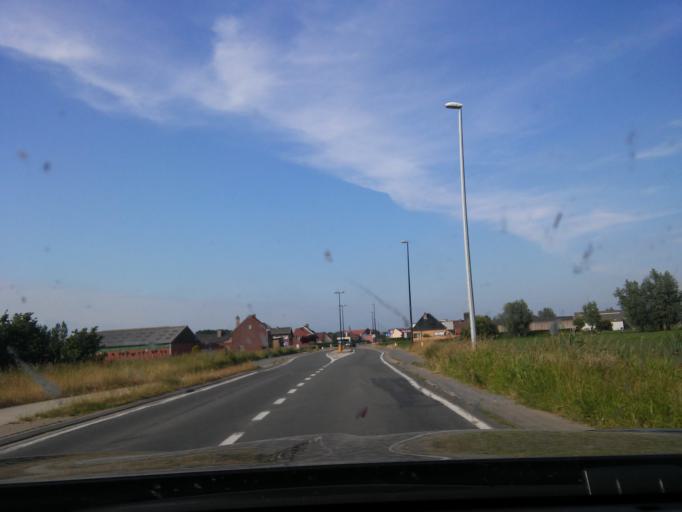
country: BE
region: Flanders
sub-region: Provincie Oost-Vlaanderen
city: Kaprijke
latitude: 51.2406
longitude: 3.5963
